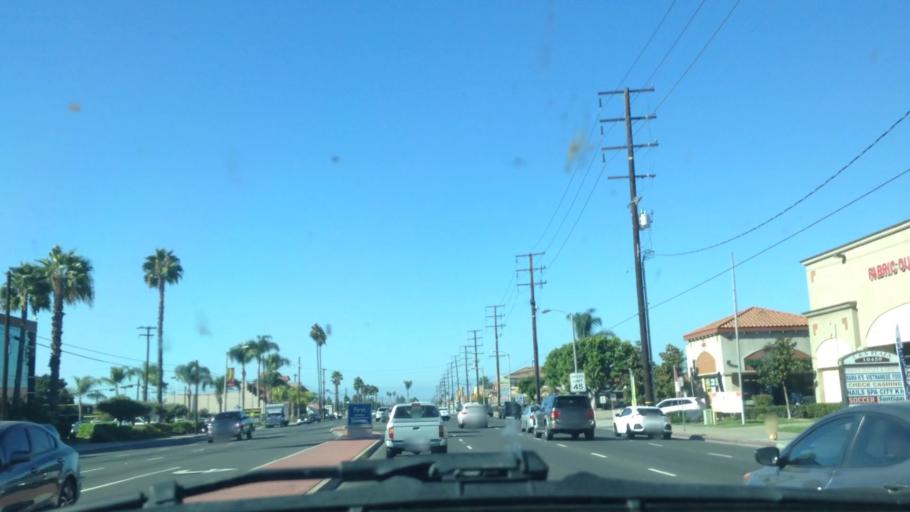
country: US
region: California
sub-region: Orange County
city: Stanton
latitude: 33.8106
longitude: -117.9932
